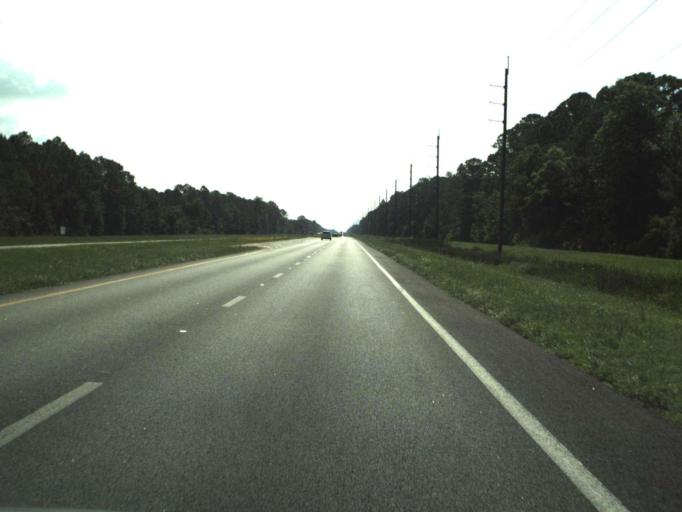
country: US
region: Florida
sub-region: Volusia County
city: Samsula-Spruce Creek
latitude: 29.0117
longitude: -81.0335
